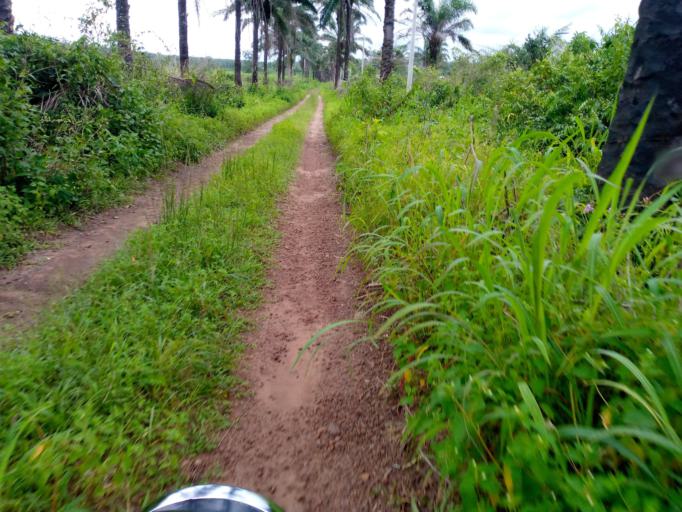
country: SL
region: Southern Province
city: Moyamba
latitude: 8.1491
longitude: -12.4420
